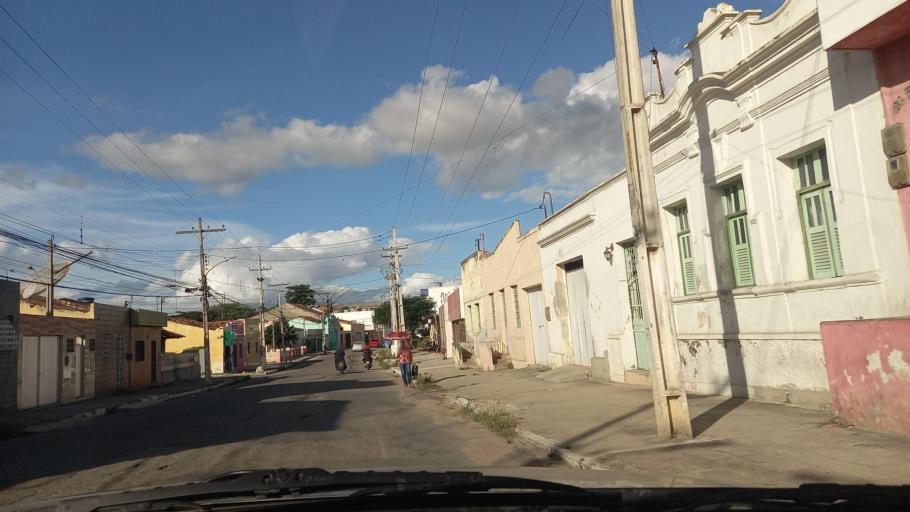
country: BR
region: Pernambuco
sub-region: Gravata
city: Gravata
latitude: -8.2044
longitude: -35.5753
